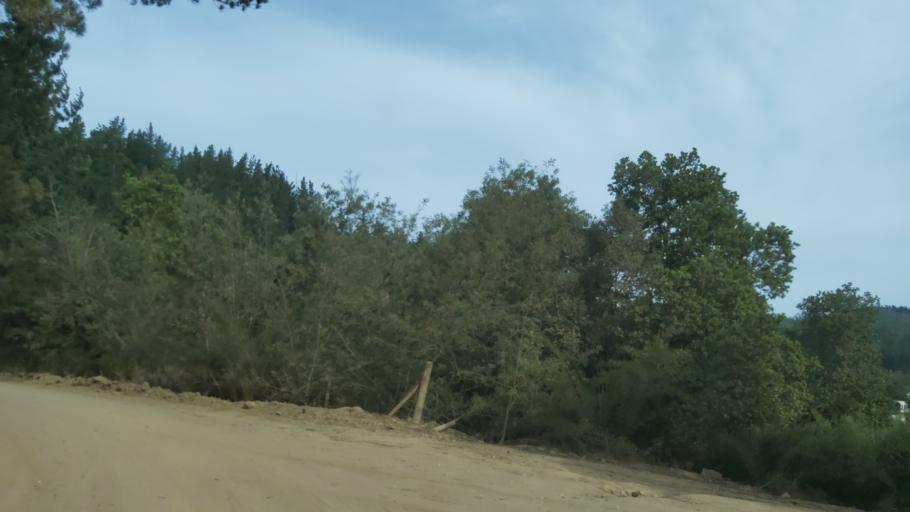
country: CL
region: Maule
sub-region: Provincia de Talca
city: Constitucion
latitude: -34.8464
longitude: -72.0403
